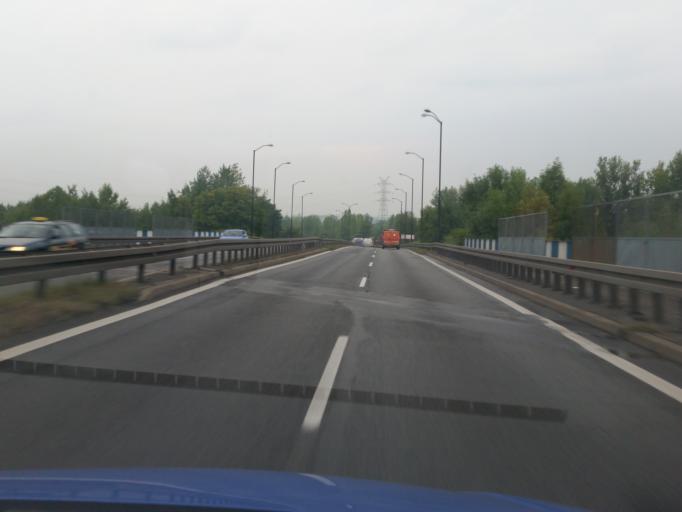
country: PL
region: Silesian Voivodeship
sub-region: Sosnowiec
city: Sosnowiec
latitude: 50.2571
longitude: 19.0800
